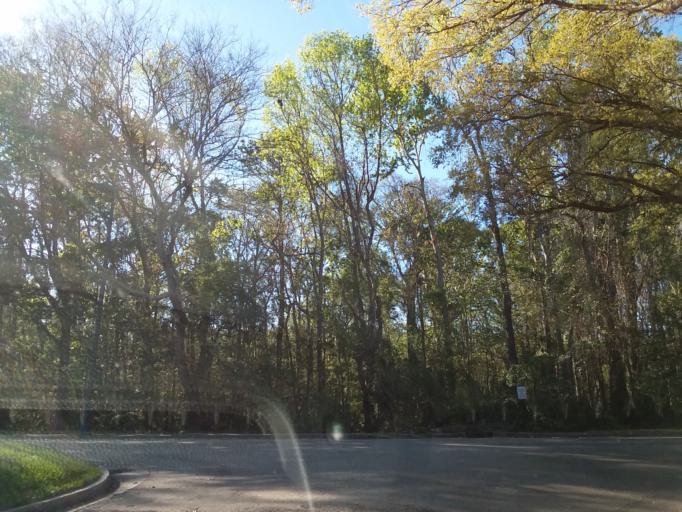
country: US
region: Florida
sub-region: Saint Johns County
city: Fruit Cove
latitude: 30.1927
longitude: -81.5552
